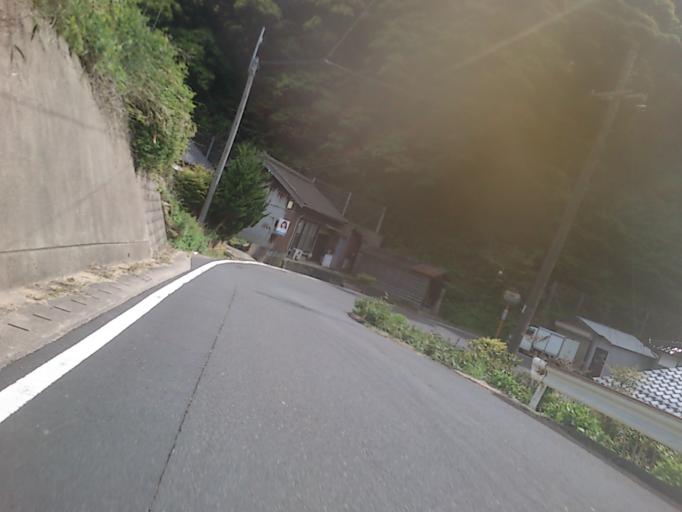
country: JP
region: Hyogo
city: Toyooka
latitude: 35.6733
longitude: 134.9716
